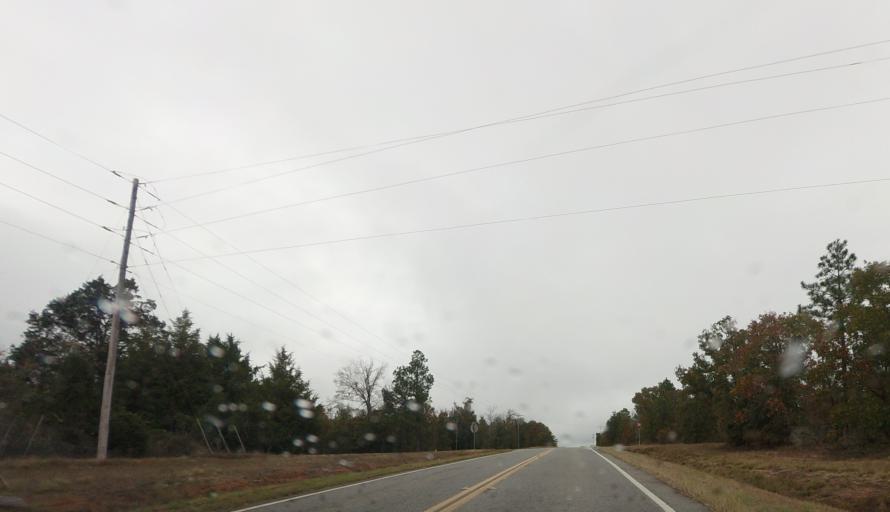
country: US
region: Georgia
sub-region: Marion County
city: Buena Vista
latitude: 32.4307
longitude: -84.3799
